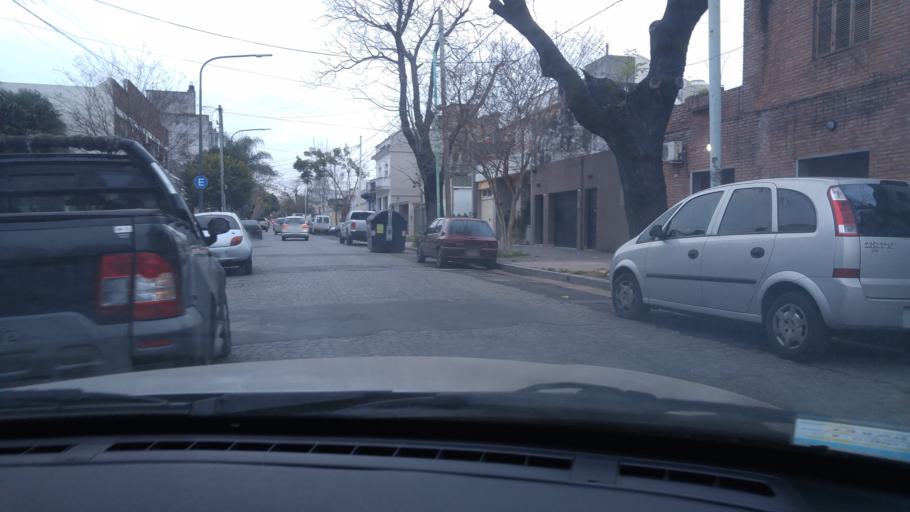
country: AR
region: Buenos Aires F.D.
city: Villa Santa Rita
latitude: -34.6317
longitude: -58.5120
